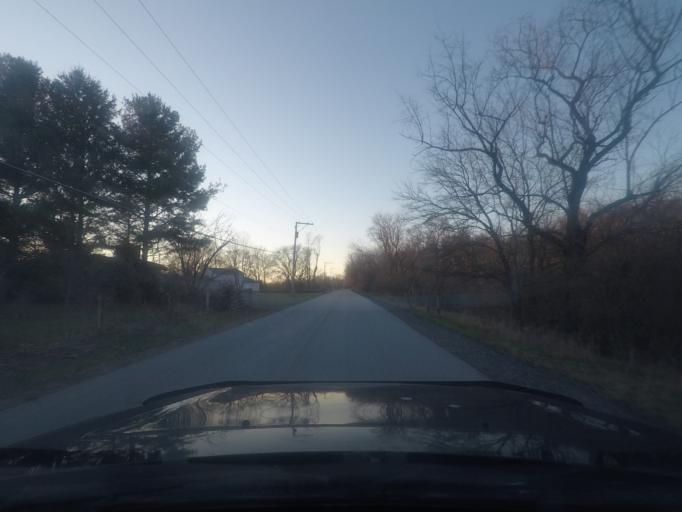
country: US
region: Indiana
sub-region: LaPorte County
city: Kingsford Heights
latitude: 41.5148
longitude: -86.6995
